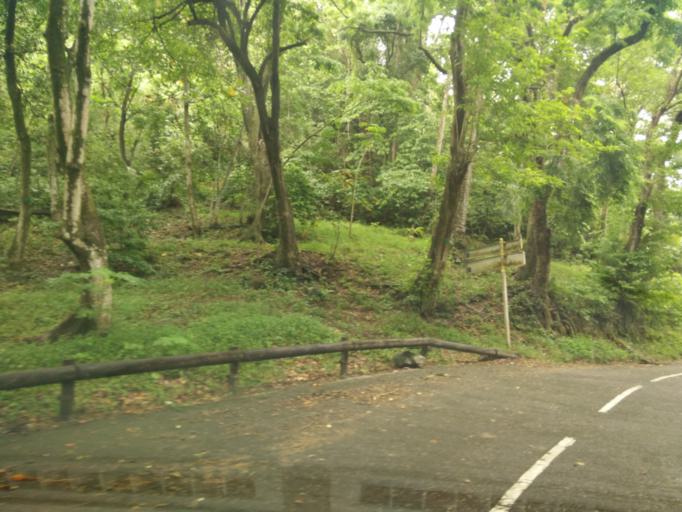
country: MQ
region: Martinique
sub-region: Martinique
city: Saint-Pierre
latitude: 14.8346
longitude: -61.2229
